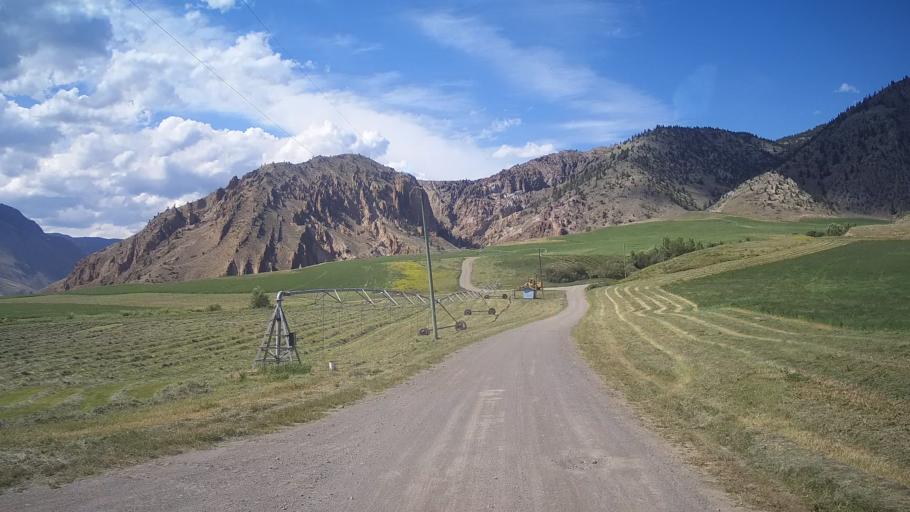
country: CA
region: British Columbia
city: Lillooet
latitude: 51.1866
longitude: -122.1184
